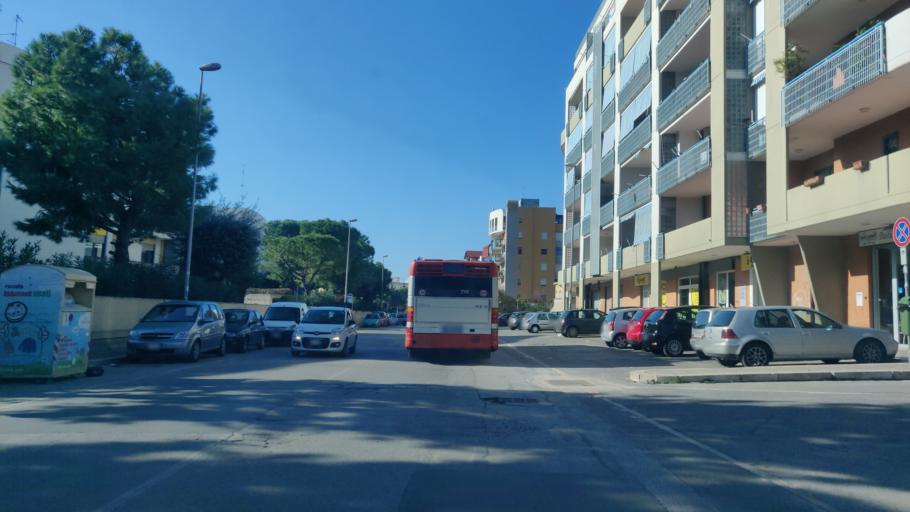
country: IT
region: Apulia
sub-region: Provincia di Bari
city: San Paolo
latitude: 41.1368
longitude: 16.8173
